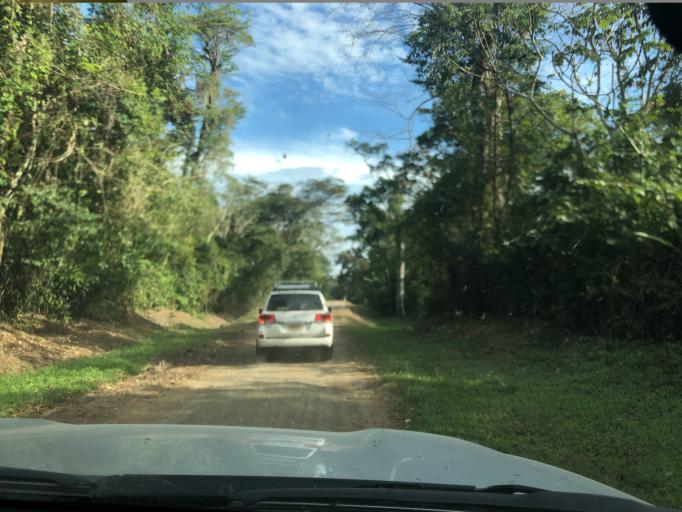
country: CR
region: Alajuela
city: San Jose
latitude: 11.1123
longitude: -85.2820
